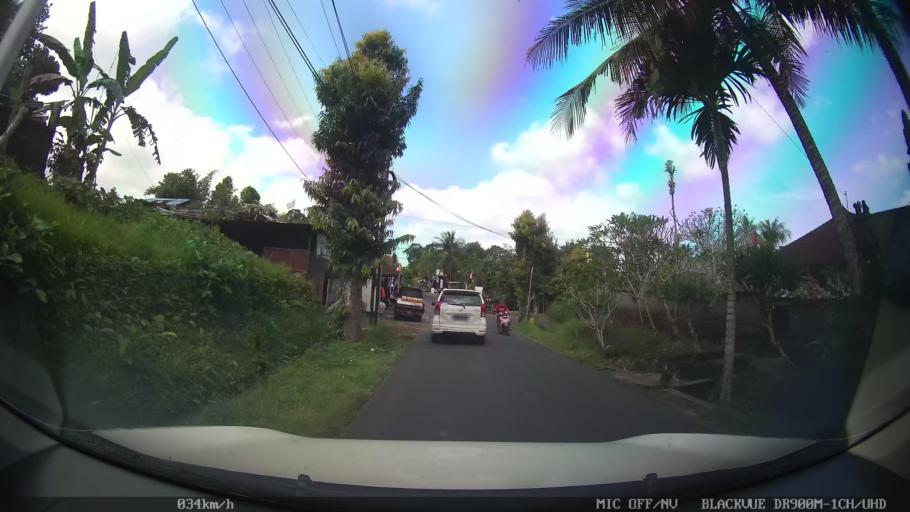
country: ID
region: Bali
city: Banjar Mulung
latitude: -8.5142
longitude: 115.3202
